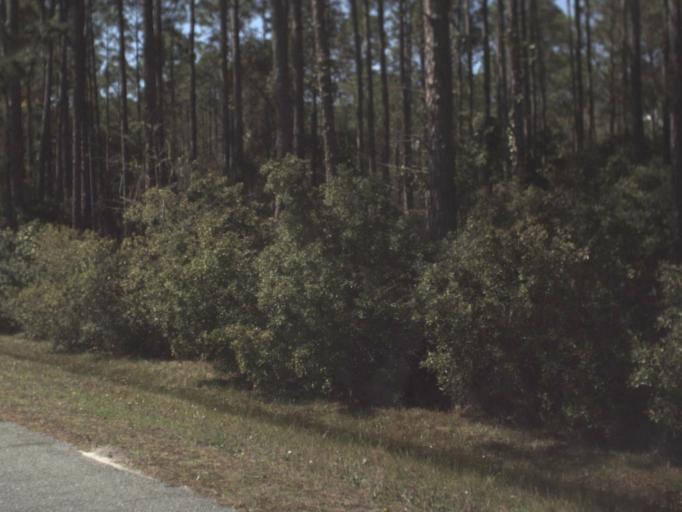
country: US
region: Florida
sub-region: Franklin County
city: Carrabelle
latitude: 29.9192
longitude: -84.5039
